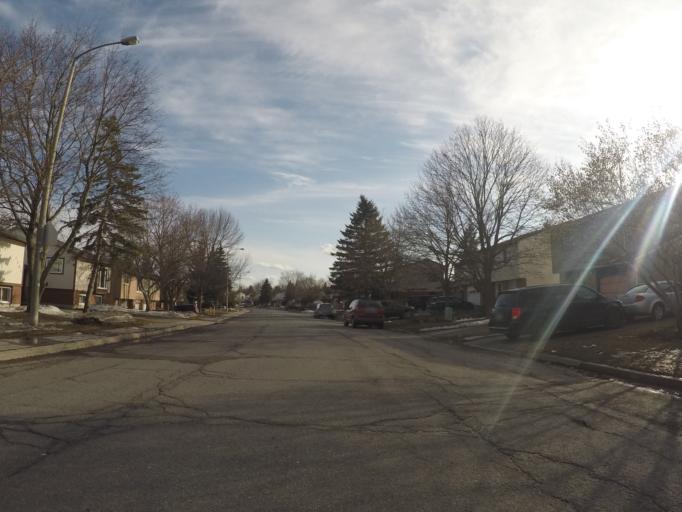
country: CA
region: Quebec
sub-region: Outaouais
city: Gatineau
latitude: 45.4666
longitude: -75.5031
